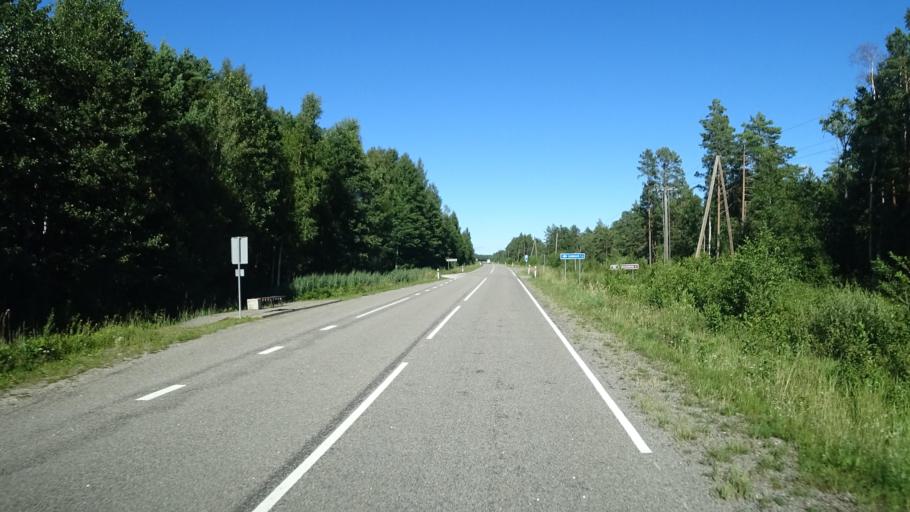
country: LV
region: Dundaga
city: Dundaga
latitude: 57.7098
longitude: 22.4451
